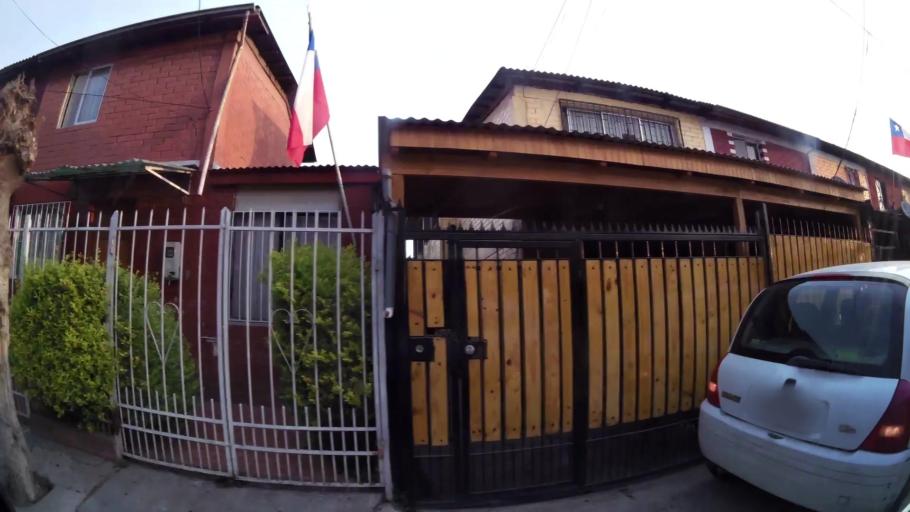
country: CL
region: Santiago Metropolitan
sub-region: Provincia de Santiago
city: Lo Prado
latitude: -33.5136
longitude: -70.7844
